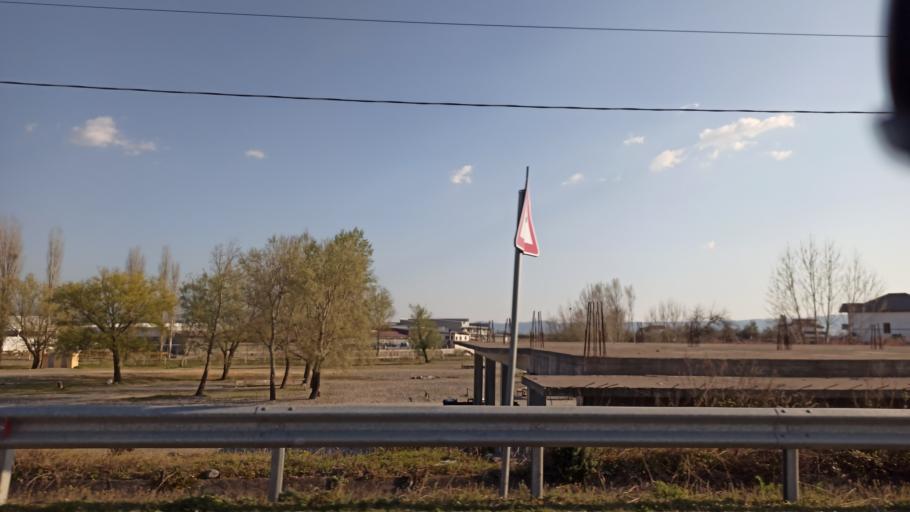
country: AL
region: Shkoder
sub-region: Rrethi i Shkodres
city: Vau i Dejes
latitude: 41.9911
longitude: 19.5995
